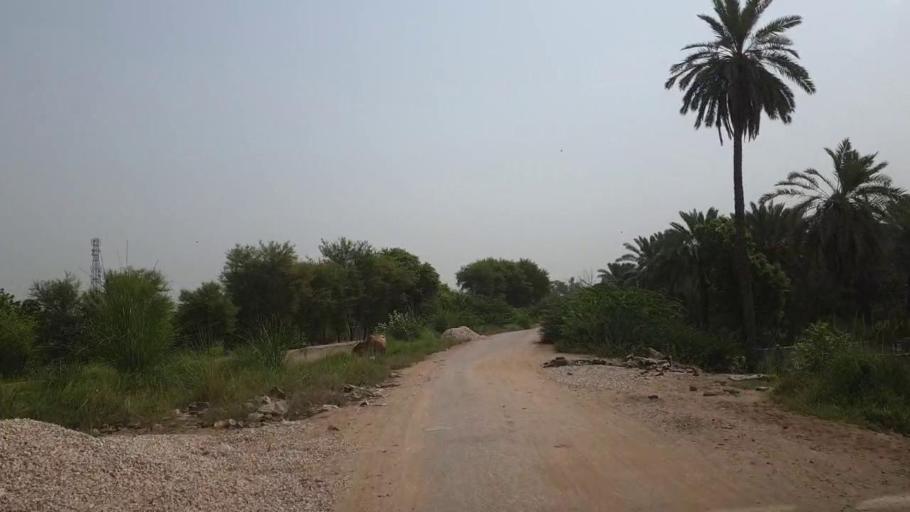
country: PK
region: Sindh
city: Gambat
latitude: 27.3815
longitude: 68.5135
